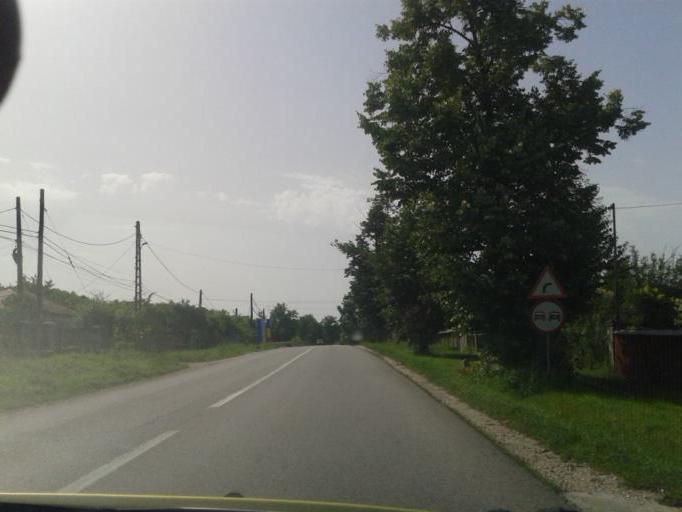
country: RO
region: Valcea
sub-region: Oras Baile Govora
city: Baile Govora
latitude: 45.0926
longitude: 24.2152
